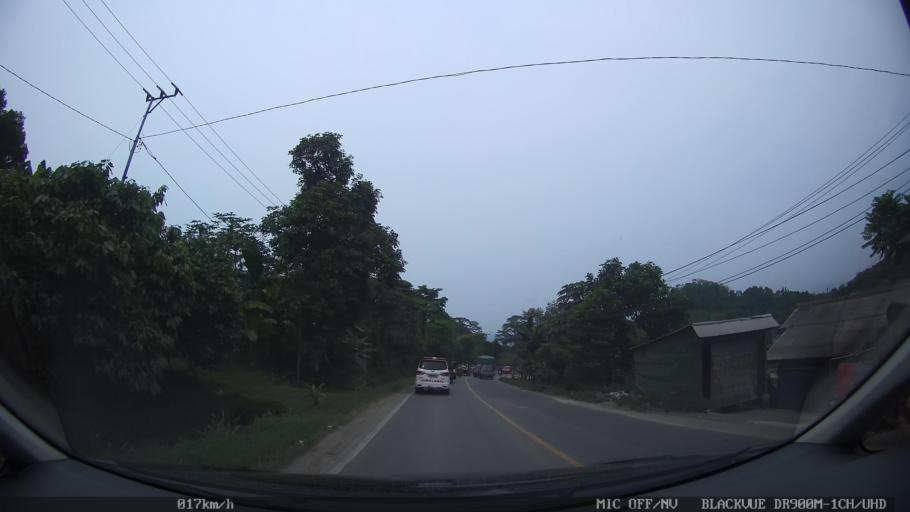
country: ID
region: Lampung
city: Panjang
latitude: -5.4381
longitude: 105.3202
